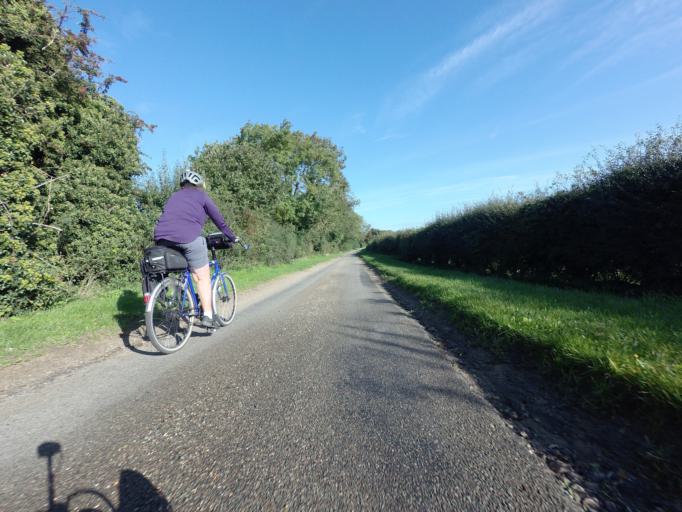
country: GB
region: England
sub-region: Norfolk
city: Dersingham
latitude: 52.8219
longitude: 0.6688
